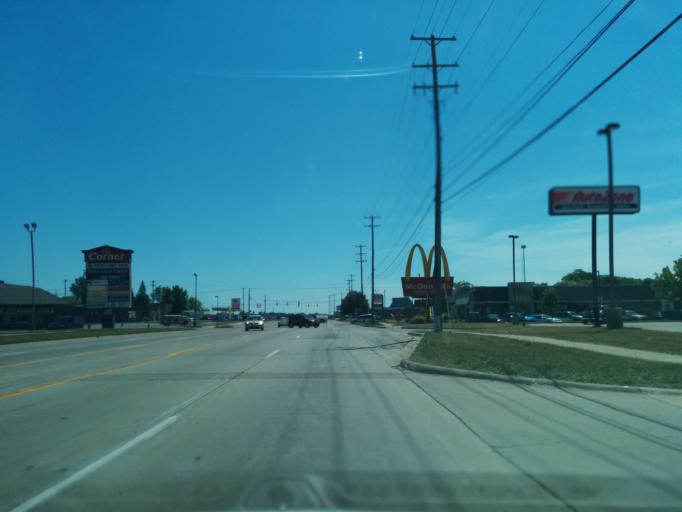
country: US
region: Michigan
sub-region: Bay County
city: Bay City
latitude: 43.6237
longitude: -83.9027
